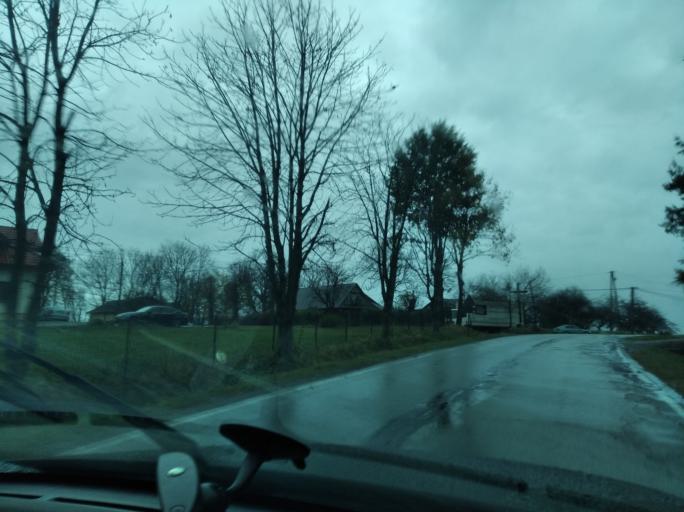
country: PL
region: Subcarpathian Voivodeship
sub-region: Powiat lancucki
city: Handzlowka
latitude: 49.9959
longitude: 22.1946
